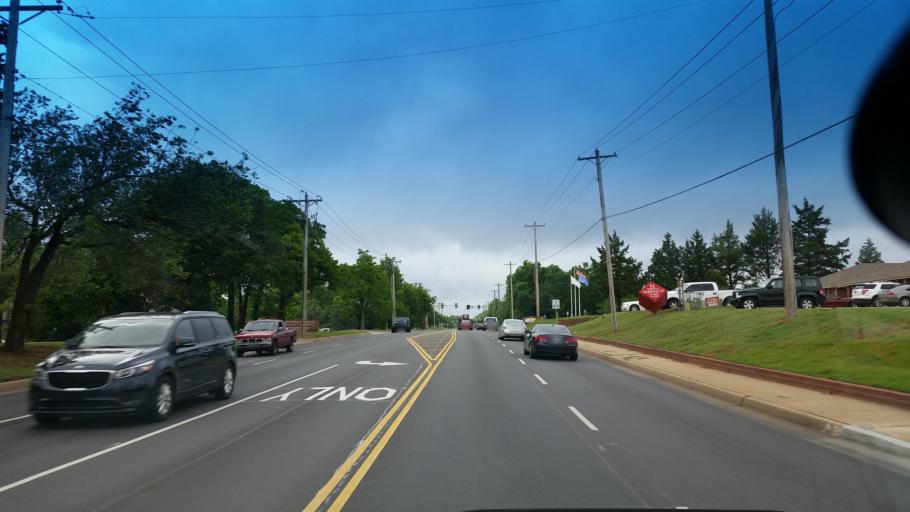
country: US
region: Oklahoma
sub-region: Oklahoma County
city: Edmond
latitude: 35.6454
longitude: -97.4605
